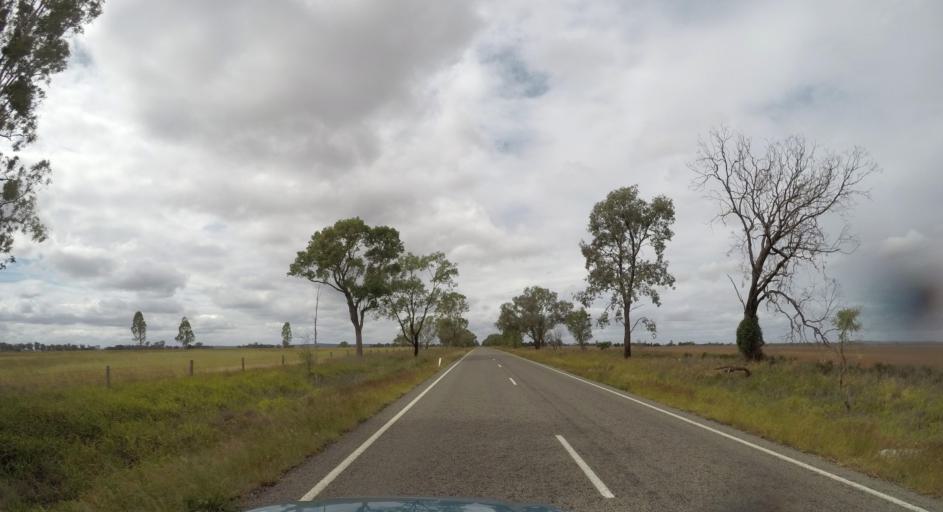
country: AU
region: Queensland
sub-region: South Burnett
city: Kingaroy
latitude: -26.3932
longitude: 151.2273
